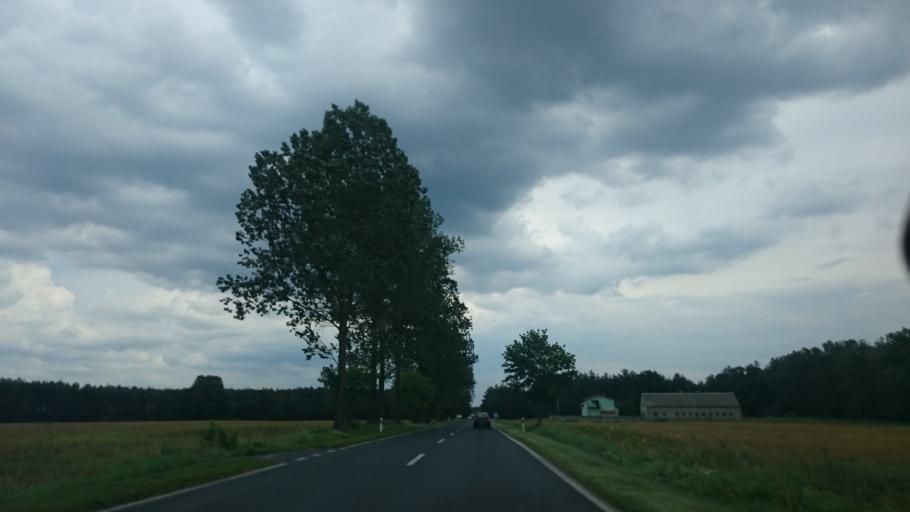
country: PL
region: Kujawsko-Pomorskie
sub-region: Powiat tucholski
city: Lubiewo
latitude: 53.4984
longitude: 18.0410
